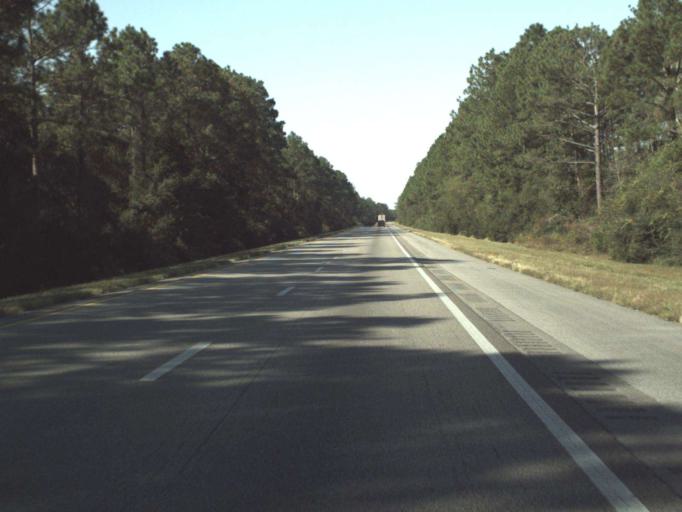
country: US
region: Florida
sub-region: Okaloosa County
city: Crestview
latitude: 30.7206
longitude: -86.4302
